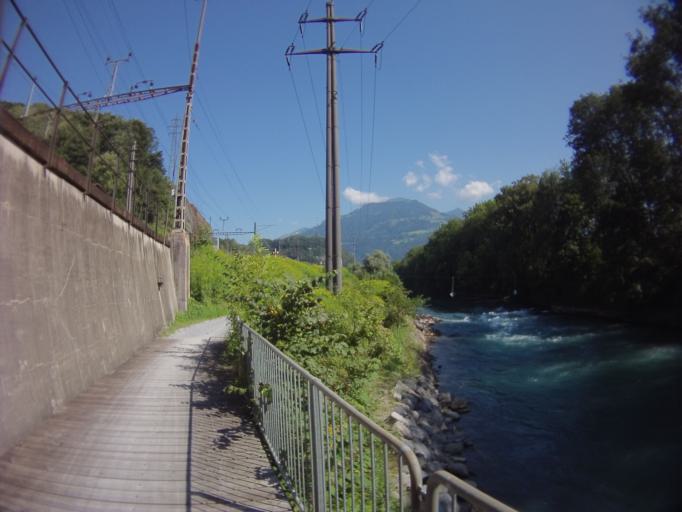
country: CH
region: Glarus
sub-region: Glarus
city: Niederurnen
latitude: 47.1393
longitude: 9.0539
